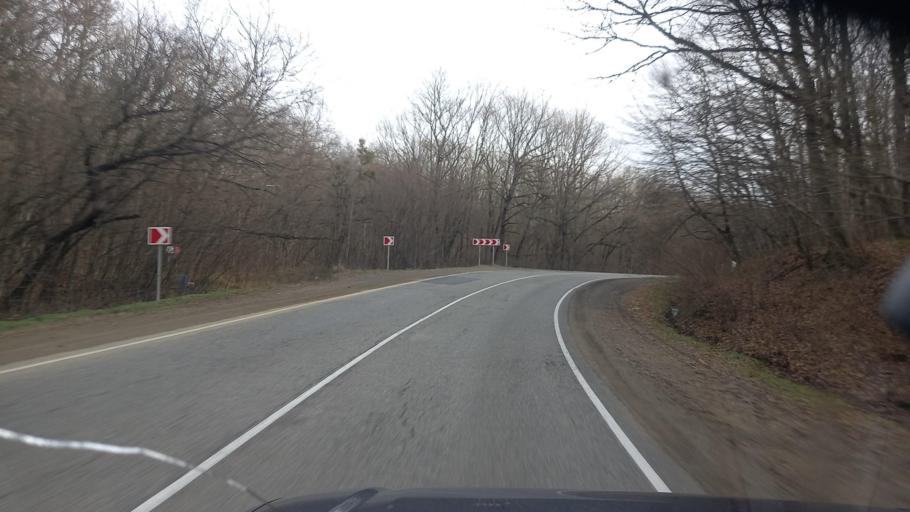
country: RU
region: Adygeya
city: Ponezhukay
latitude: 44.6659
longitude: 39.4729
